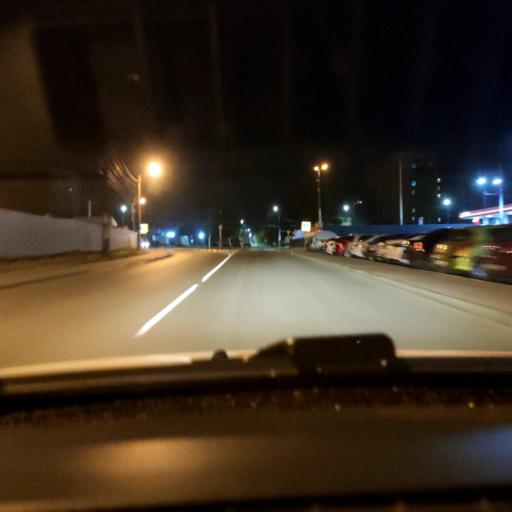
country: RU
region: Voronezj
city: Voronezh
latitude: 51.7008
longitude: 39.1637
